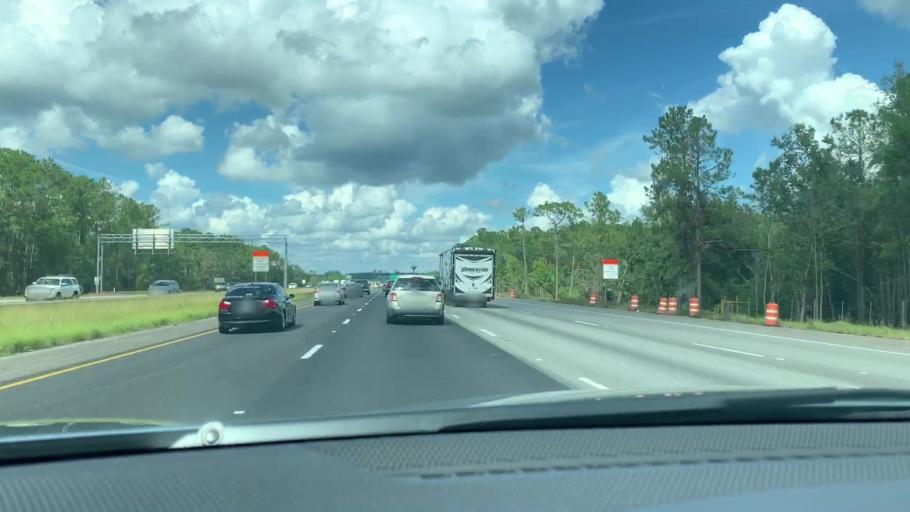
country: US
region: Georgia
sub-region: Camden County
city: Kingsland
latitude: 30.8303
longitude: -81.6675
